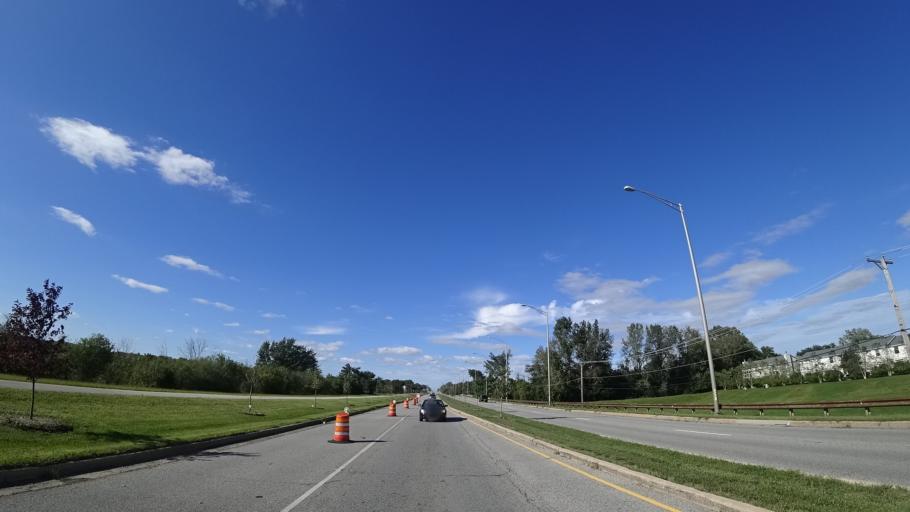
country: US
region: Illinois
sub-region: Cook County
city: Oak Forest
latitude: 41.5907
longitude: -87.7361
